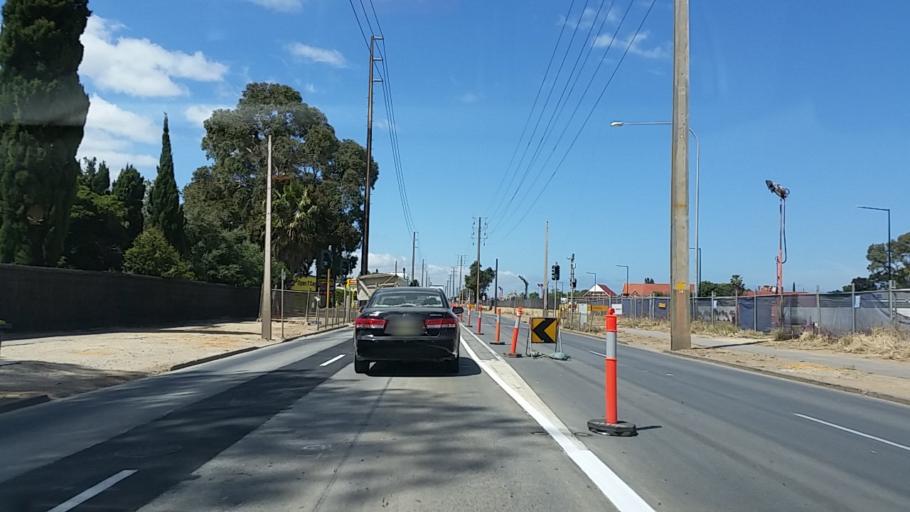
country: AU
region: South Australia
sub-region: Charles Sturt
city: Allenby Gardens
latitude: -34.8930
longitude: 138.5688
